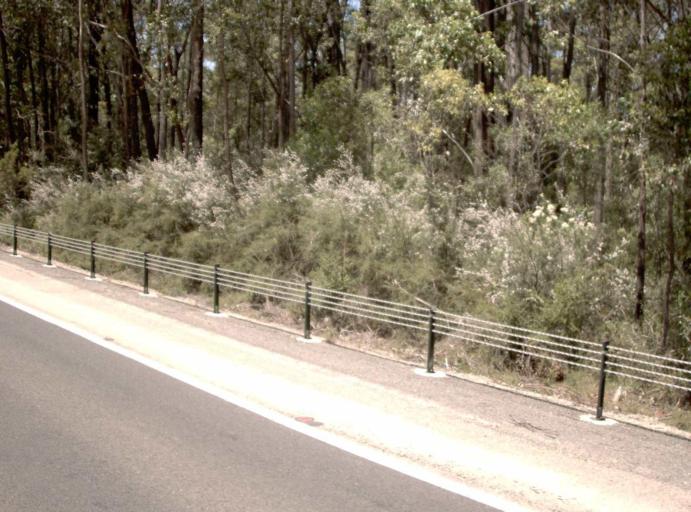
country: AU
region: Victoria
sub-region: East Gippsland
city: Lakes Entrance
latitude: -37.7020
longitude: 148.5838
